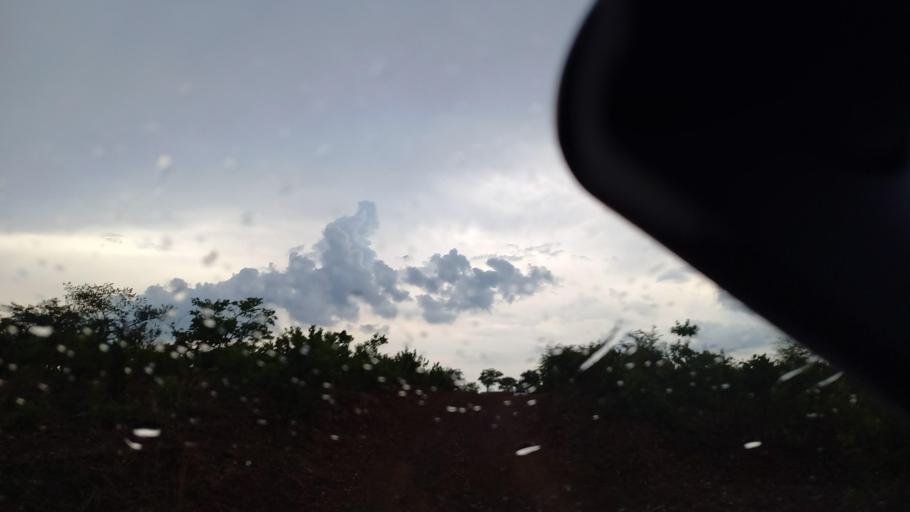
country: ZM
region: Lusaka
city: Kafue
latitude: -15.9730
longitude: 28.2518
